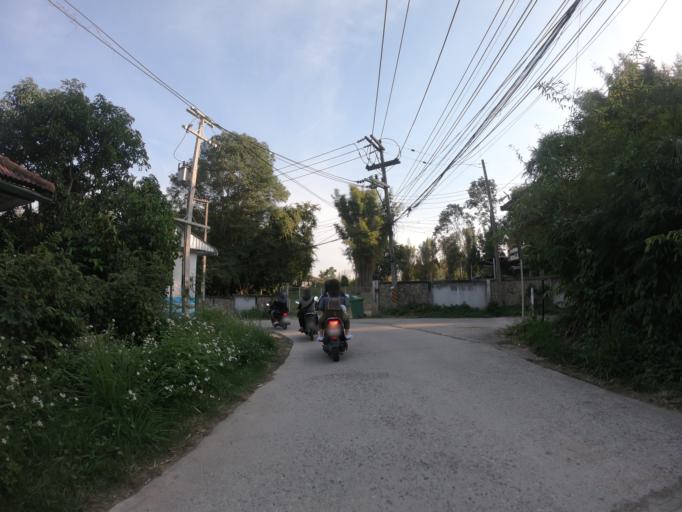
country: TH
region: Chiang Mai
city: Chiang Mai
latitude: 18.8200
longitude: 98.9493
